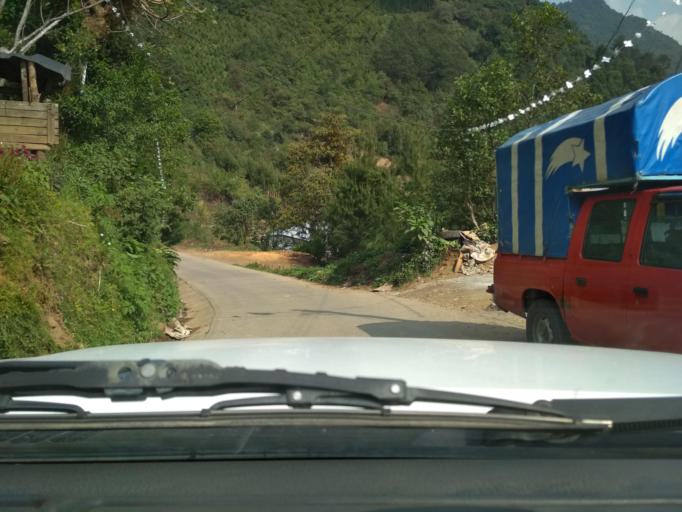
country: MX
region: Veracruz
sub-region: Camerino Z. Mendoza
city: Necoxtla
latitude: 18.7705
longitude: -97.1543
